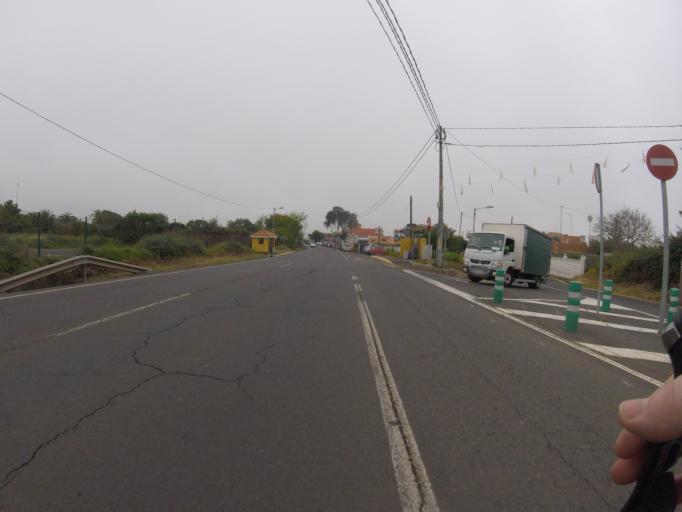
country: ES
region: Canary Islands
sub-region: Provincia de Santa Cruz de Tenerife
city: Tacoronte
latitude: 28.4922
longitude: -16.3665
